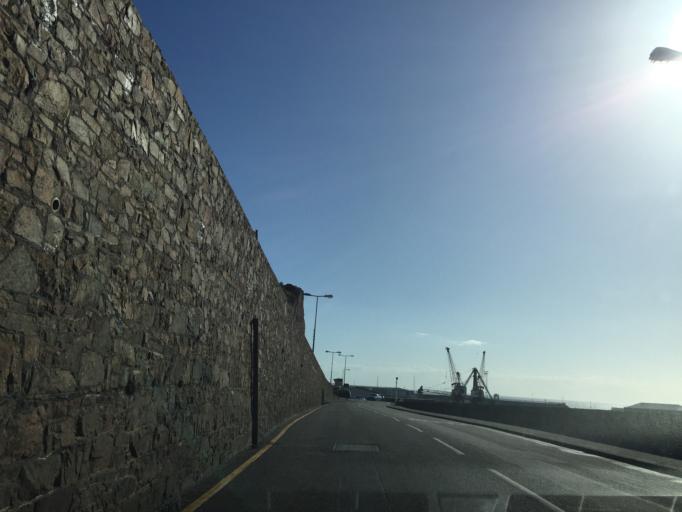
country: JE
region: St Helier
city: Saint Helier
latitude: 49.1780
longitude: -2.1095
